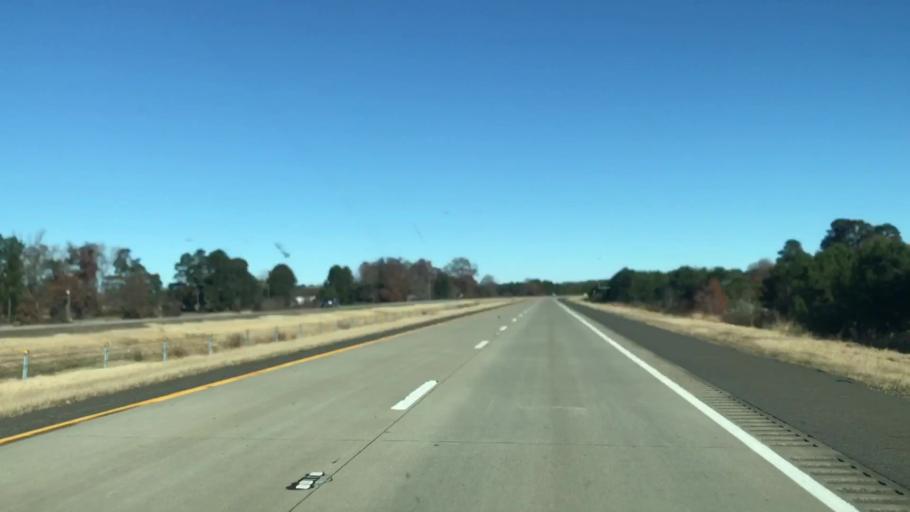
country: US
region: Texas
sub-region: Cass County
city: Queen City
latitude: 33.1955
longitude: -93.8774
